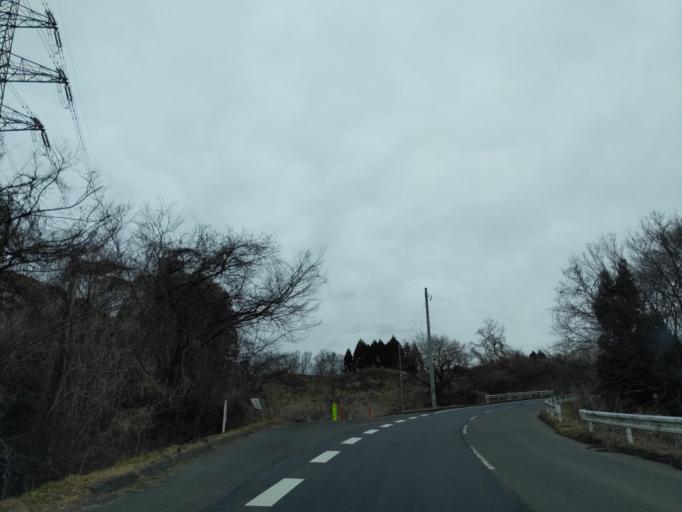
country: JP
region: Fukushima
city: Miharu
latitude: 37.4677
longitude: 140.4527
